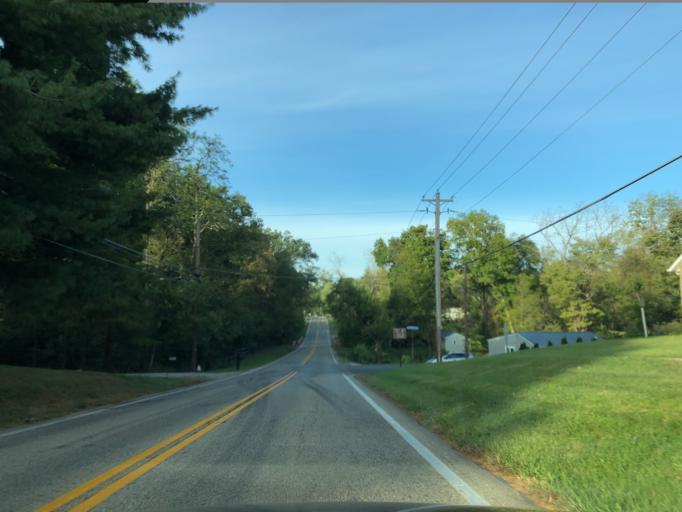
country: US
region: Ohio
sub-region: Warren County
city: Loveland Park
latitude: 39.2859
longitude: -84.2694
